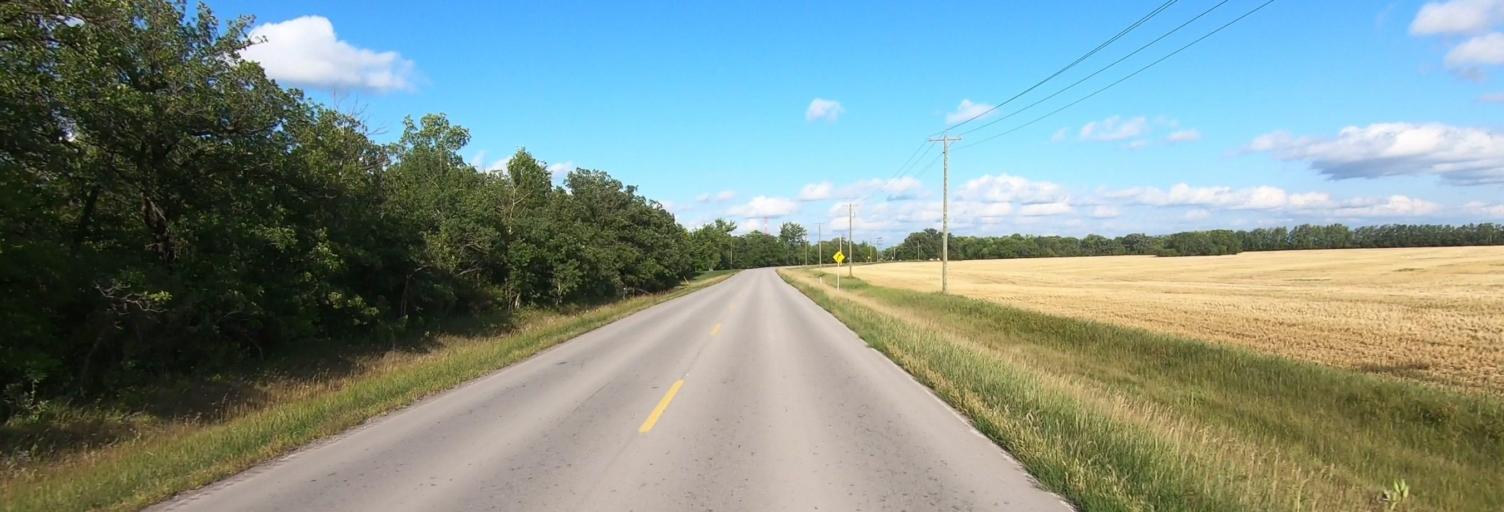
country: CA
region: Manitoba
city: Selkirk
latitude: 50.1217
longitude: -96.8707
